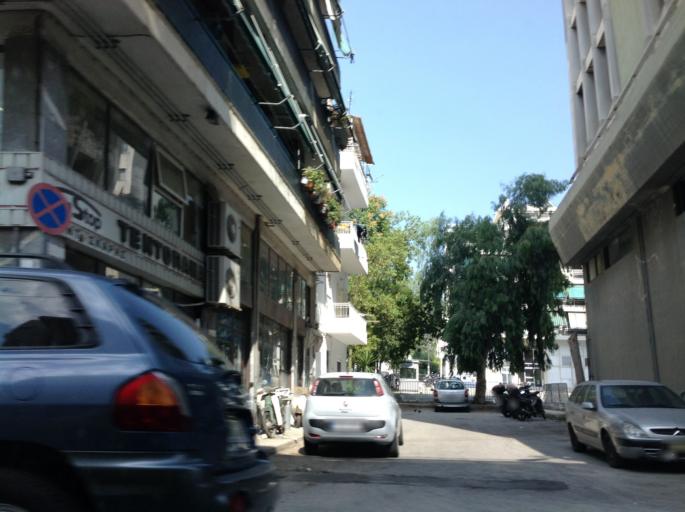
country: GR
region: Attica
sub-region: Nomarchia Athinas
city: Vyronas
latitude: 37.9712
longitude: 23.7548
